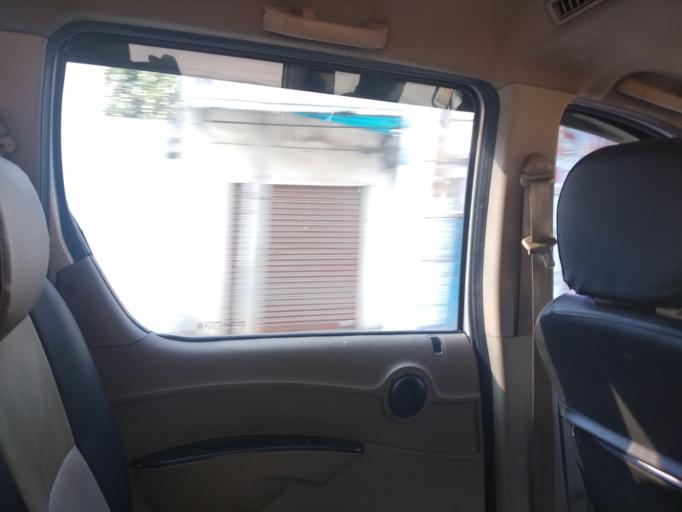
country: IN
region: Telangana
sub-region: Rangareddi
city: Kukatpalli
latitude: 17.4569
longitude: 78.4401
